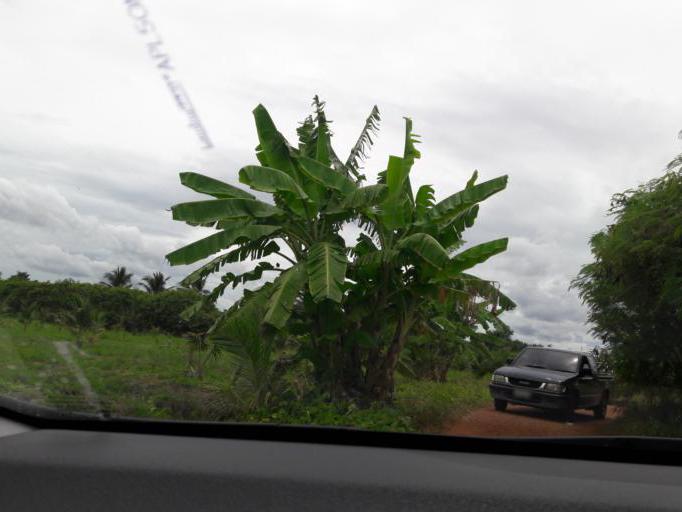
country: TH
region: Samut Sakhon
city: Ban Phaeo
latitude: 13.5499
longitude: 100.0436
